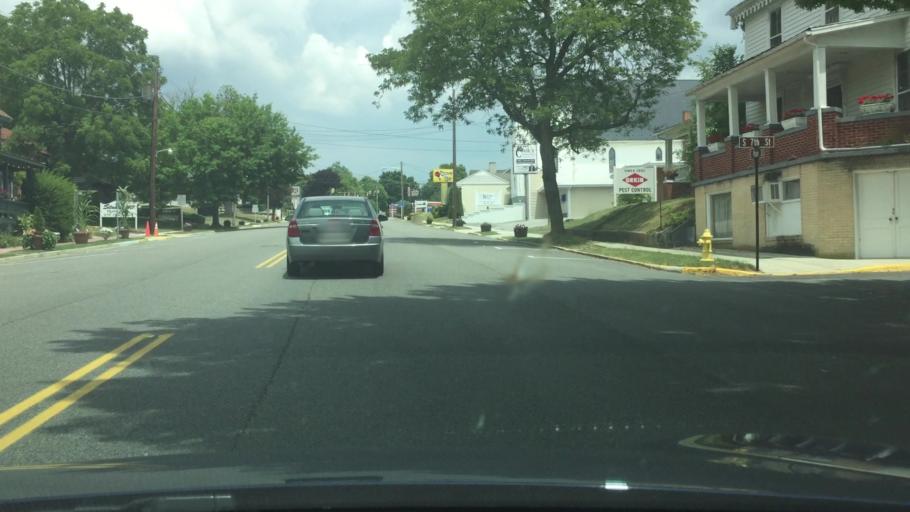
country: US
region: Virginia
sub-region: Wythe County
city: Wytheville
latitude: 36.9525
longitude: -81.0800
